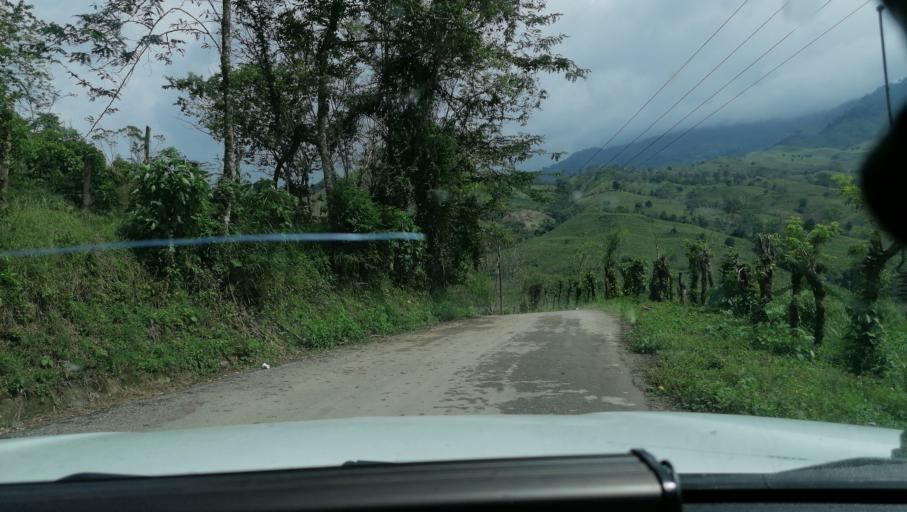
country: MX
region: Chiapas
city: Ocotepec
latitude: 17.3113
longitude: -93.1757
